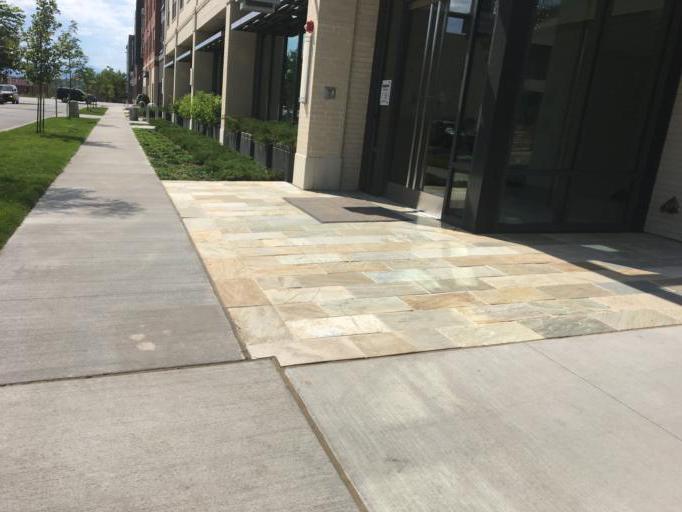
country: US
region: Colorado
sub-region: Denver County
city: Denver
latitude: 39.6949
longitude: -104.9863
